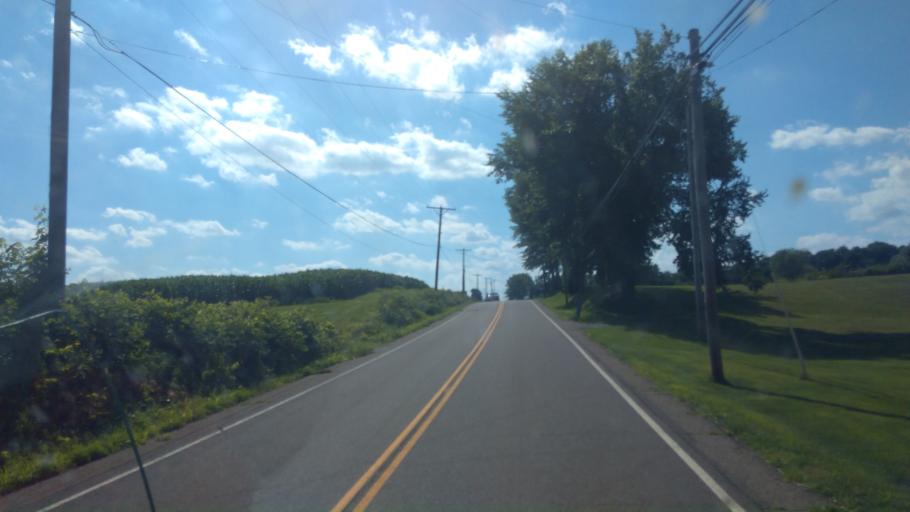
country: US
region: Ohio
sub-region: Stark County
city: Navarre
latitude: 40.7255
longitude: -81.5410
